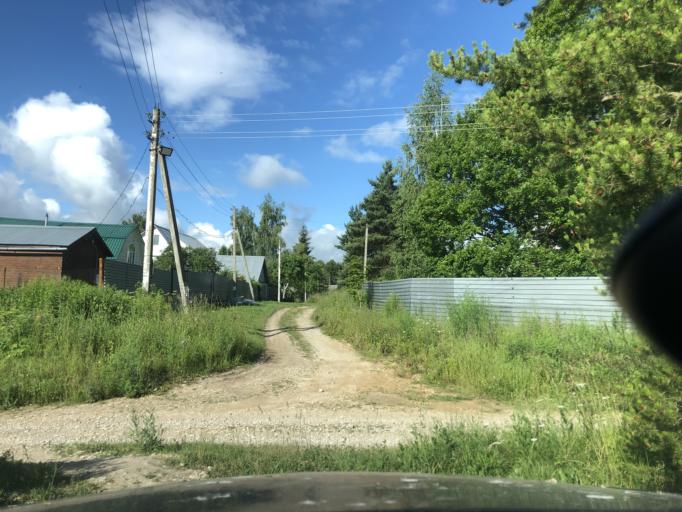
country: RU
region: Tula
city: Shvartsevskiy
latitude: 54.2580
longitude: 37.9137
